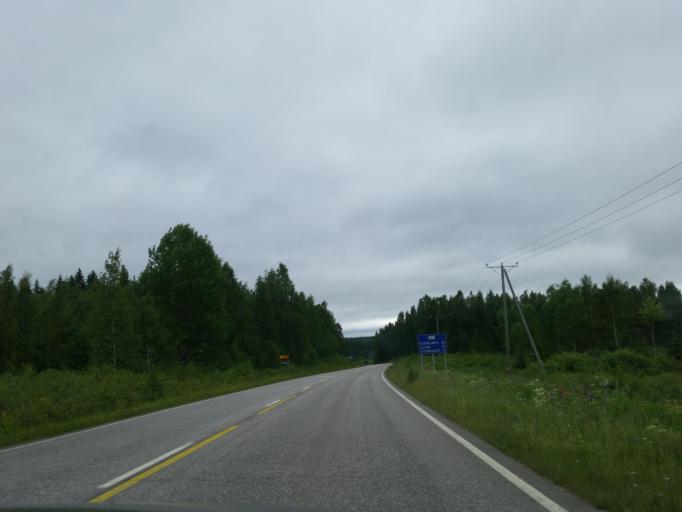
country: FI
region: Northern Savo
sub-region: Koillis-Savo
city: Kaavi
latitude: 62.9728
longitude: 28.5043
